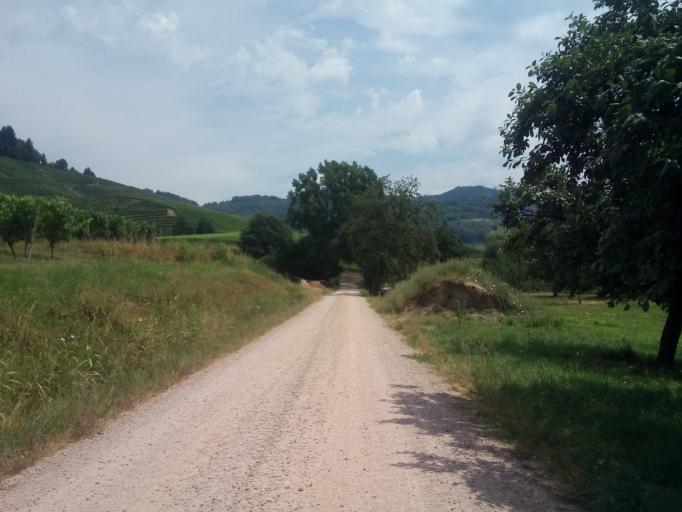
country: DE
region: Baden-Wuerttemberg
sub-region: Freiburg Region
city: Kappelrodeck
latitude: 48.6023
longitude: 8.1061
